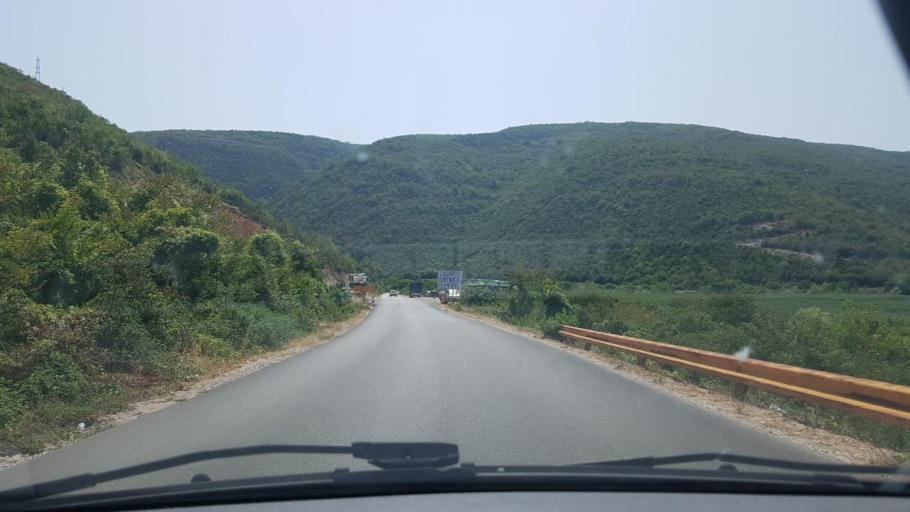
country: BA
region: Federation of Bosnia and Herzegovina
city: Tasovcici
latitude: 43.0175
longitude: 17.7817
